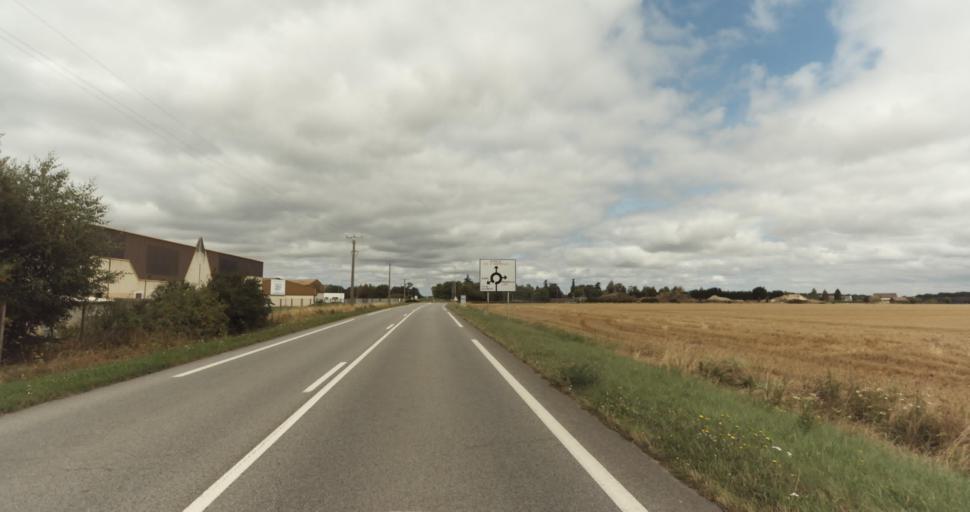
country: FR
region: Haute-Normandie
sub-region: Departement de l'Eure
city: Evreux
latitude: 48.9815
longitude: 1.1578
